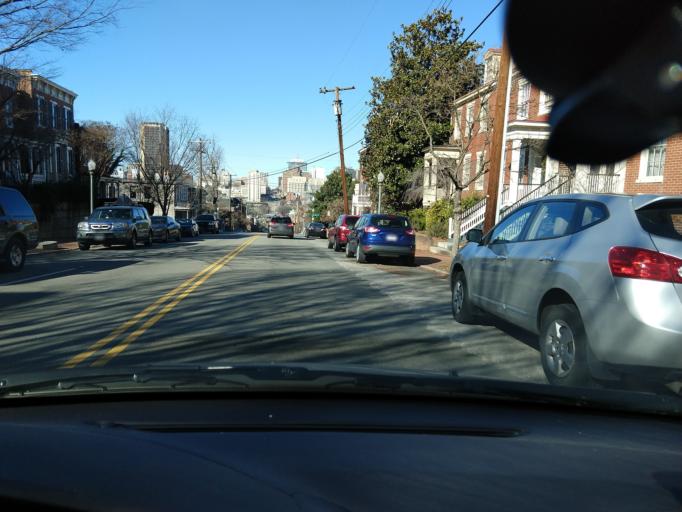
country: US
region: Virginia
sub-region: Henrico County
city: Montrose
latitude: 37.5330
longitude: -77.4209
